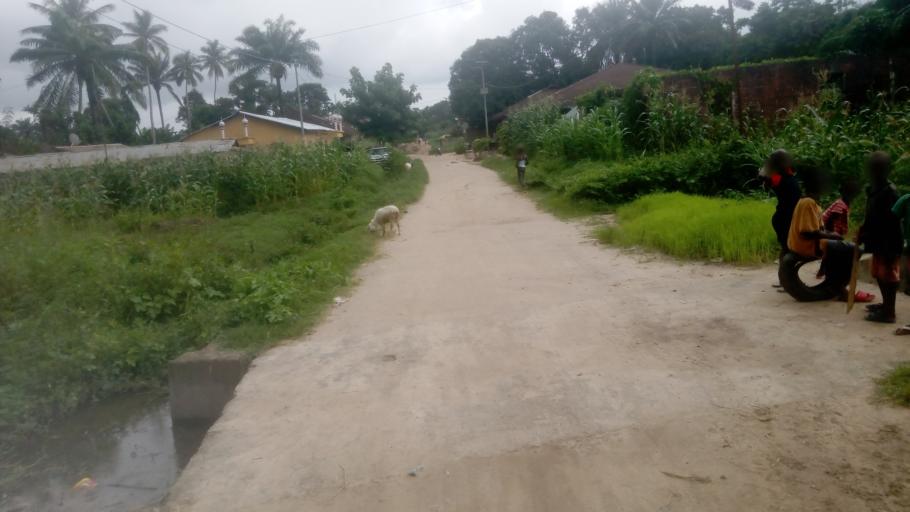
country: SL
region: Northern Province
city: Lunsar
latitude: 8.6815
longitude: -12.5375
